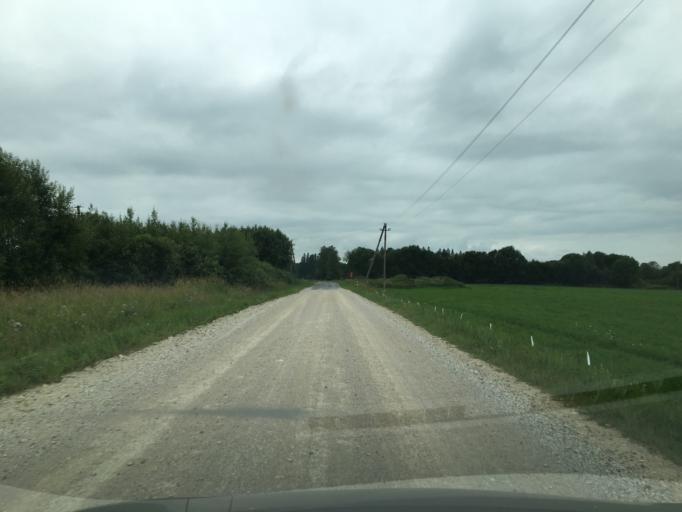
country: EE
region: Raplamaa
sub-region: Jaervakandi vald
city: Jarvakandi
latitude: 58.7938
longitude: 24.9395
